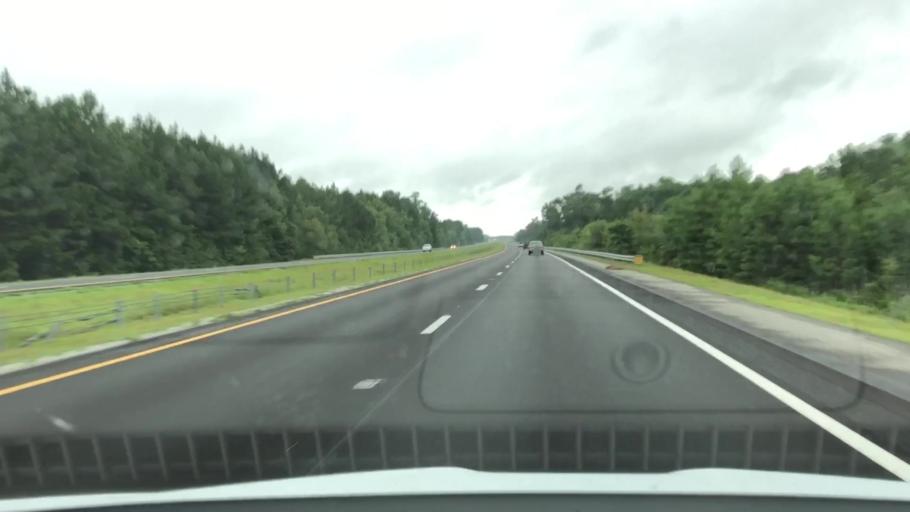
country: US
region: North Carolina
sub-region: Wayne County
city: Goldsboro
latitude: 35.4528
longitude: -77.9843
